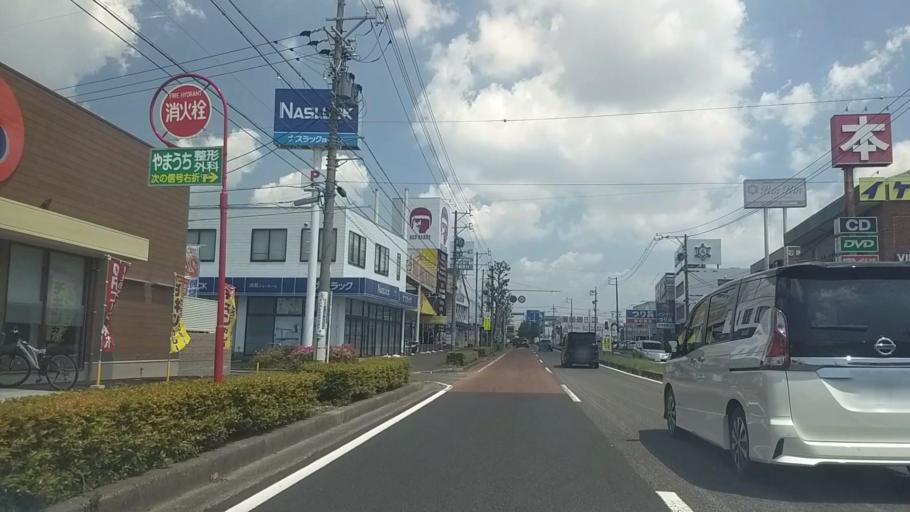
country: JP
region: Shizuoka
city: Hamamatsu
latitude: 34.7300
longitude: 137.7329
